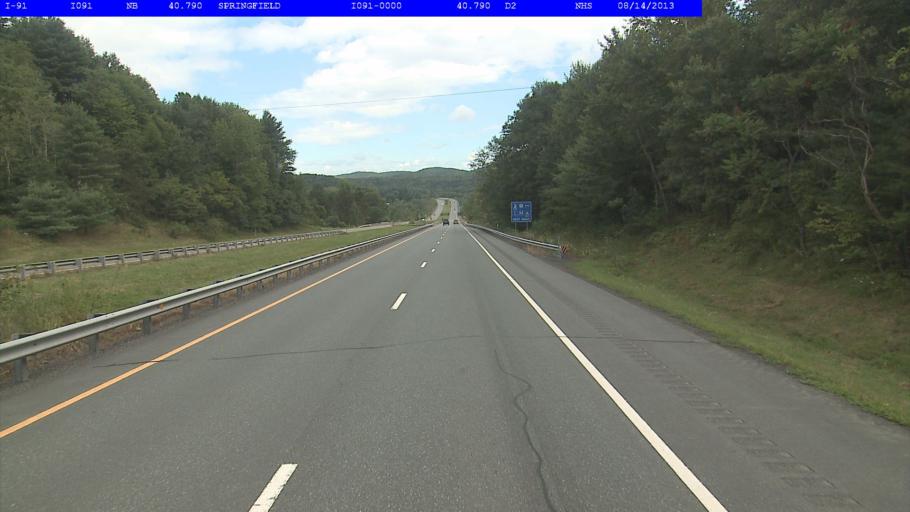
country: US
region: New Hampshire
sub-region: Sullivan County
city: Charlestown
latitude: 43.2551
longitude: -72.4401
